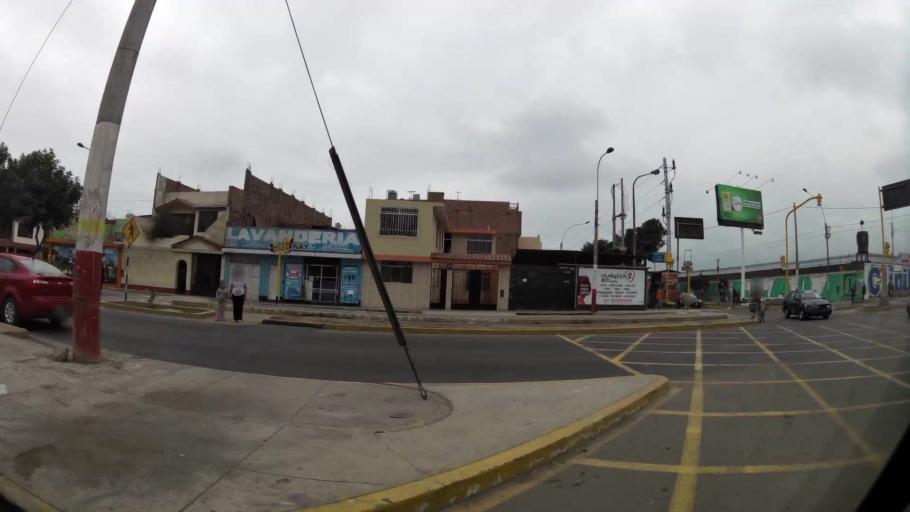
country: PE
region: Callao
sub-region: Callao
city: Callao
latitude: -12.0551
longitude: -77.1061
